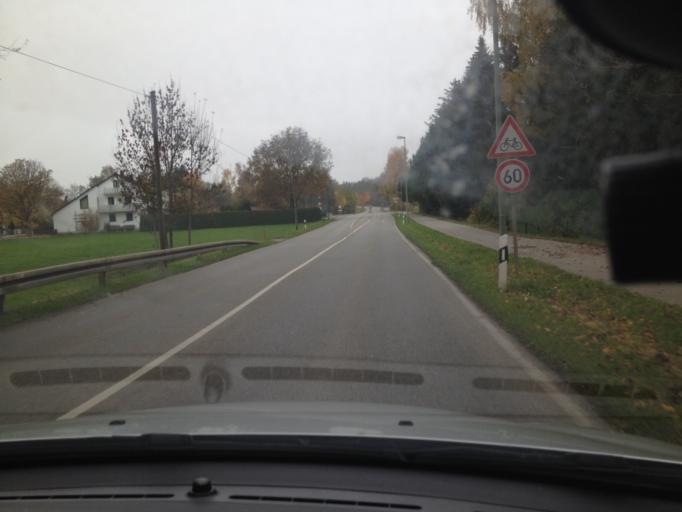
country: DE
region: Bavaria
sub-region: Swabia
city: Schwabmunchen
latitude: 48.1751
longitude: 10.7373
